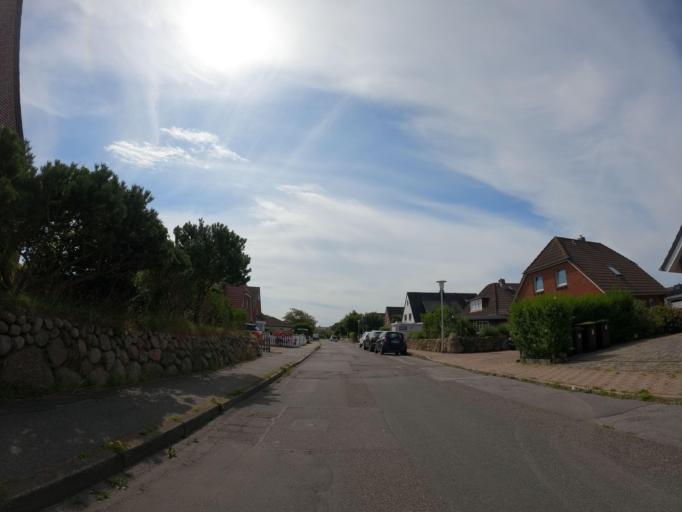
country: DE
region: Schleswig-Holstein
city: Westerland
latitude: 54.9157
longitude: 8.3115
